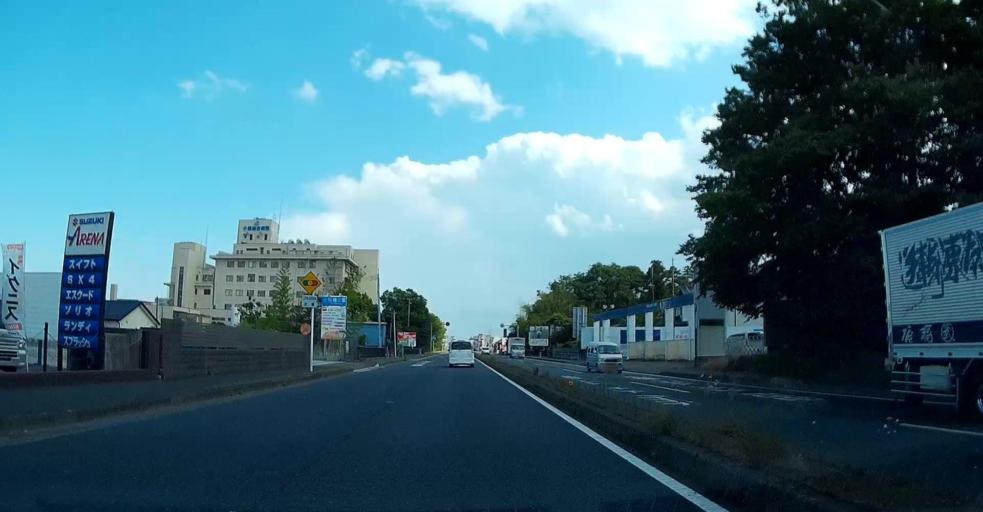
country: JP
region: Chiba
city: Noda
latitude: 35.9529
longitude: 139.8780
